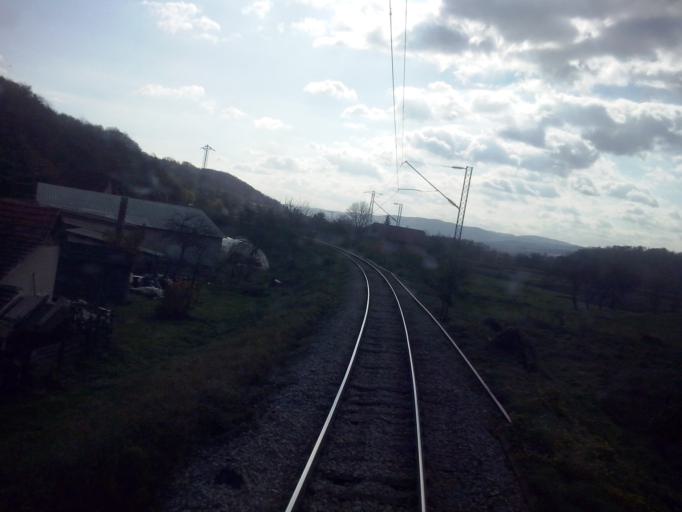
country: RS
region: Central Serbia
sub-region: Zlatiborski Okrug
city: Pozega
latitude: 43.8930
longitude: 19.9959
